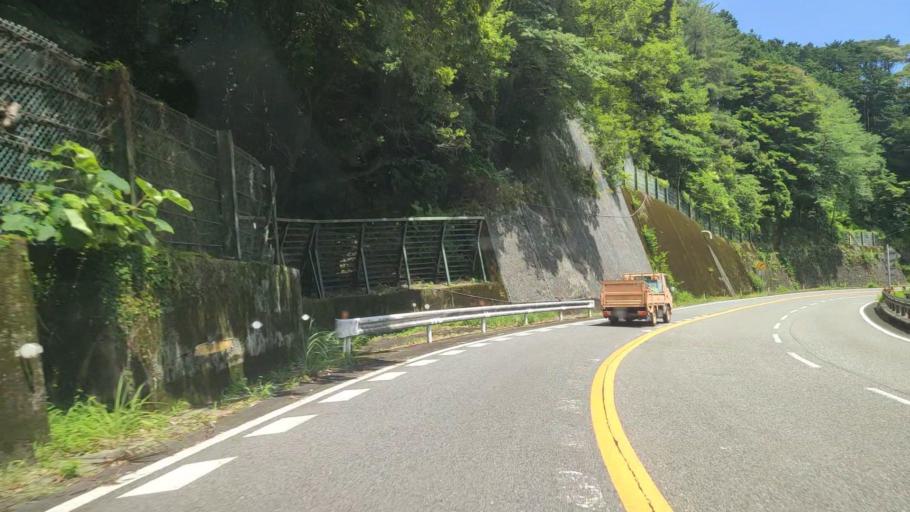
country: JP
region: Mie
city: Owase
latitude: 33.9201
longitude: 136.1025
